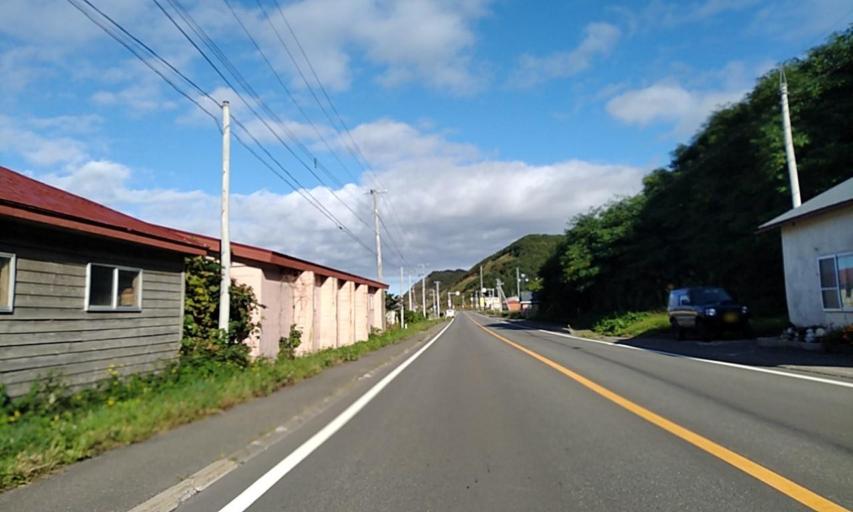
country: JP
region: Hokkaido
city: Shizunai-furukawacho
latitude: 42.2032
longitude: 142.6577
